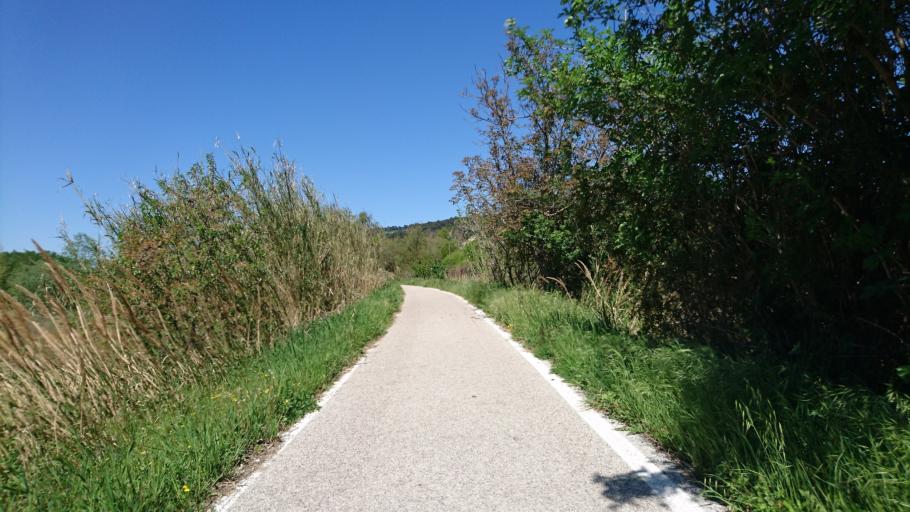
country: IT
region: The Marches
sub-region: Provincia di Pesaro e Urbino
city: Pesaro
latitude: 43.9050
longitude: 12.8830
